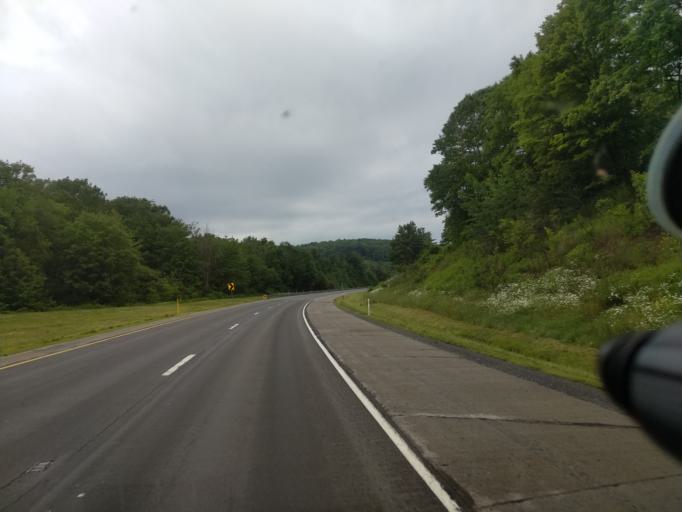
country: US
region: Pennsylvania
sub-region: Union County
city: Mifflinburg
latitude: 41.0416
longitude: -77.1386
